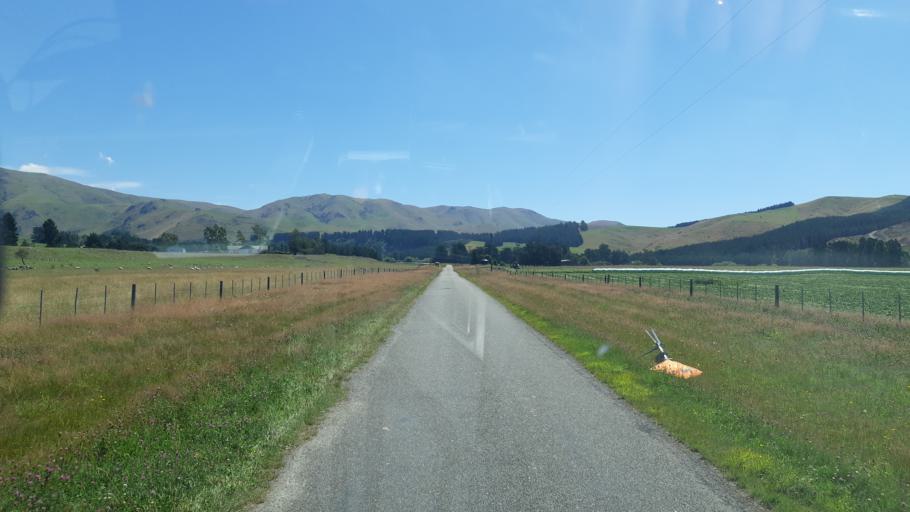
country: NZ
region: Canterbury
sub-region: Timaru District
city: Pleasant Point
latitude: -44.3347
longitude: 170.8900
